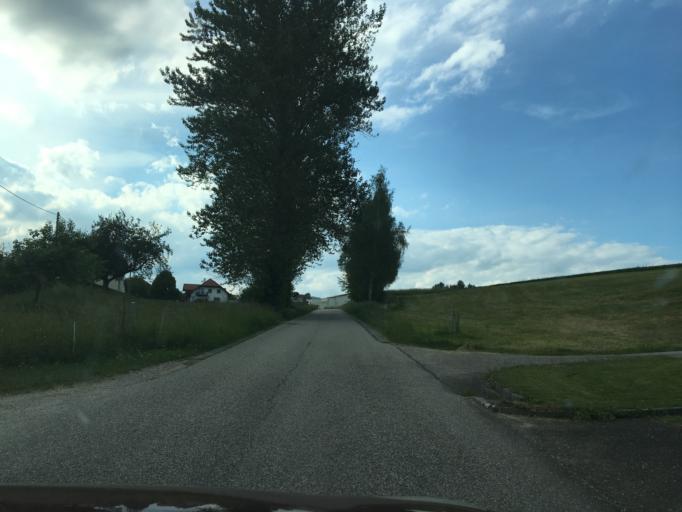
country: AT
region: Upper Austria
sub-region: Politischer Bezirk Urfahr-Umgebung
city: Bad Leonfelden
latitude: 48.5169
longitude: 14.3084
